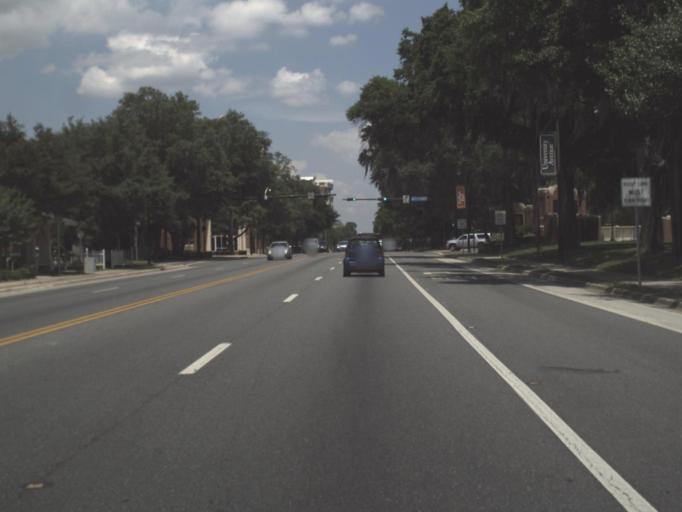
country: US
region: Florida
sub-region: Alachua County
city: Gainesville
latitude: 29.6521
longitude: -82.3508
